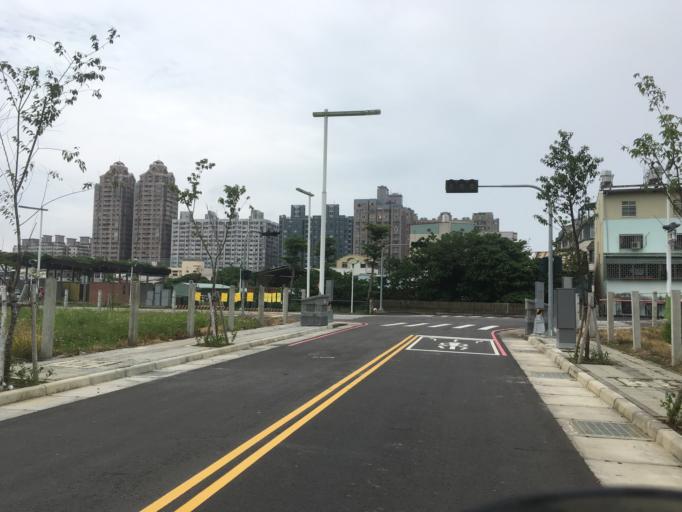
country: TW
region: Taiwan
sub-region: Taichung City
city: Taichung
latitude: 24.1909
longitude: 120.7063
